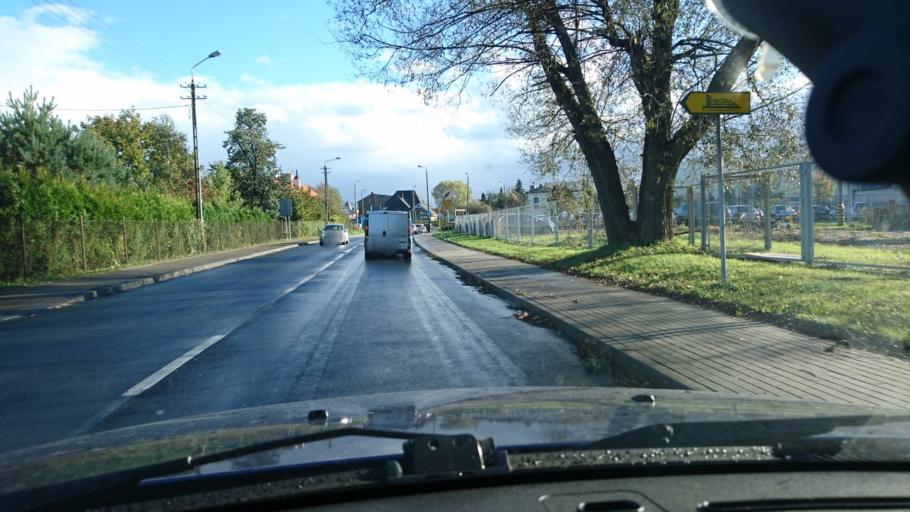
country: PL
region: Silesian Voivodeship
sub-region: Bielsko-Biala
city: Bielsko-Biala
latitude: 49.8418
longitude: 19.0511
